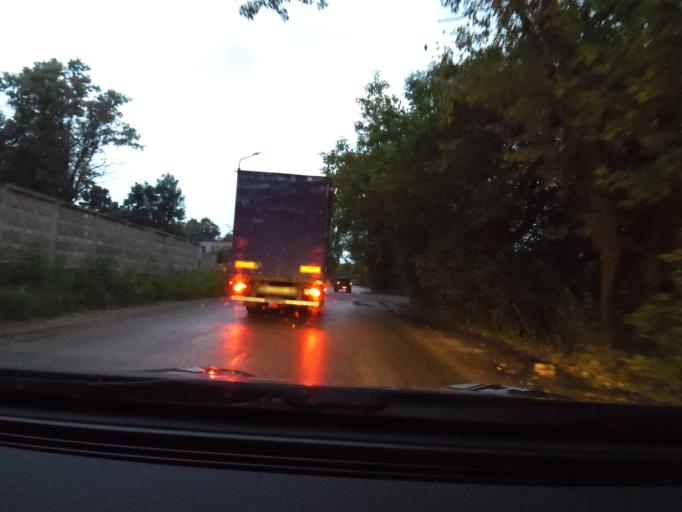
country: RU
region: Vladimir
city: Aleksandrov
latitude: 56.3994
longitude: 38.7332
